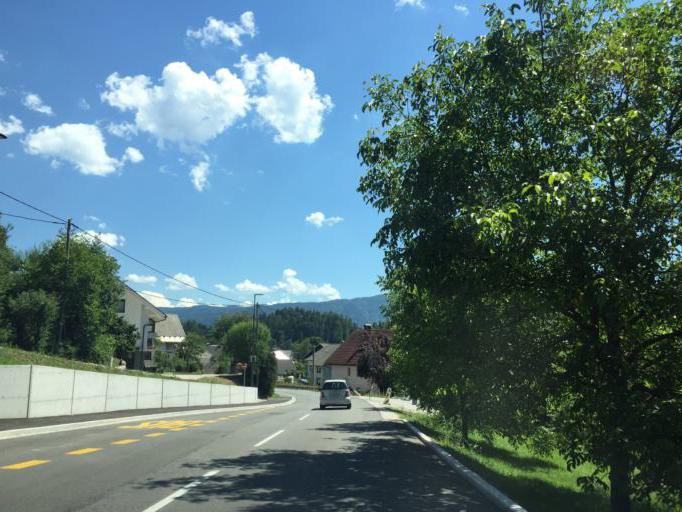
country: SI
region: Gorje
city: Zgornje Gorje
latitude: 46.3786
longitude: 14.0874
